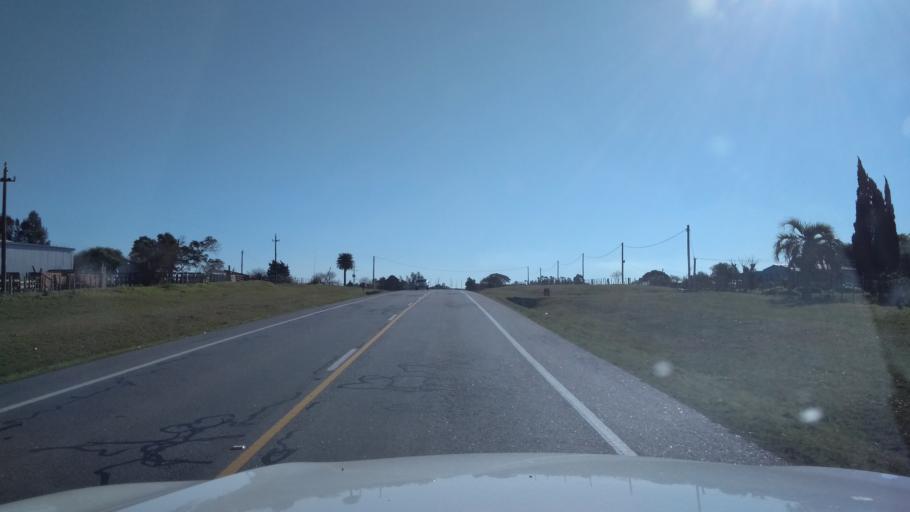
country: UY
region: Canelones
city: San Jacinto
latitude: -34.5315
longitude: -55.9440
